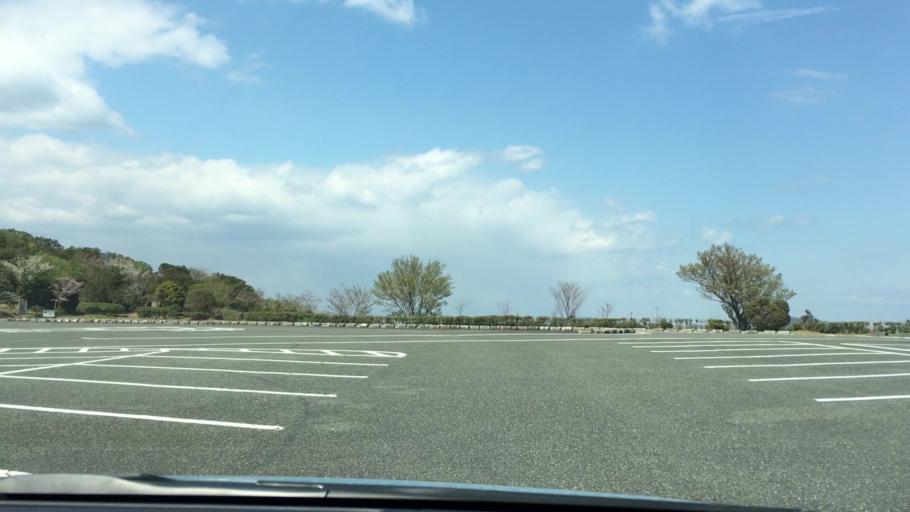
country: JP
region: Mie
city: Toba
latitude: 34.4272
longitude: 136.9143
